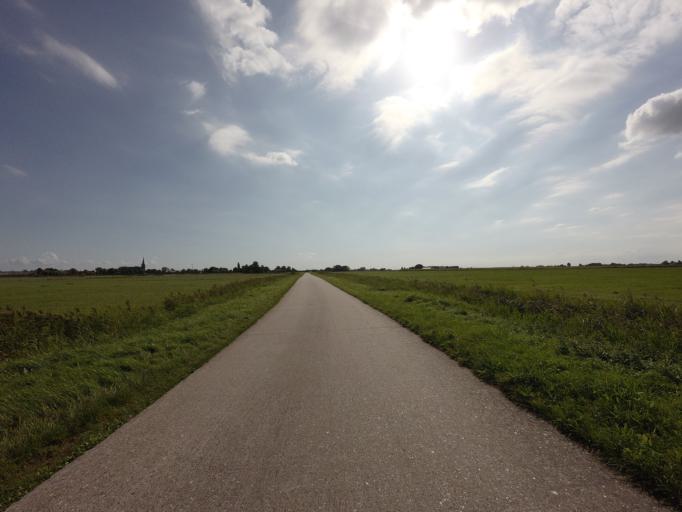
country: NL
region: Friesland
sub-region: Gemeente Littenseradiel
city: Makkum
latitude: 53.0826
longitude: 5.6319
